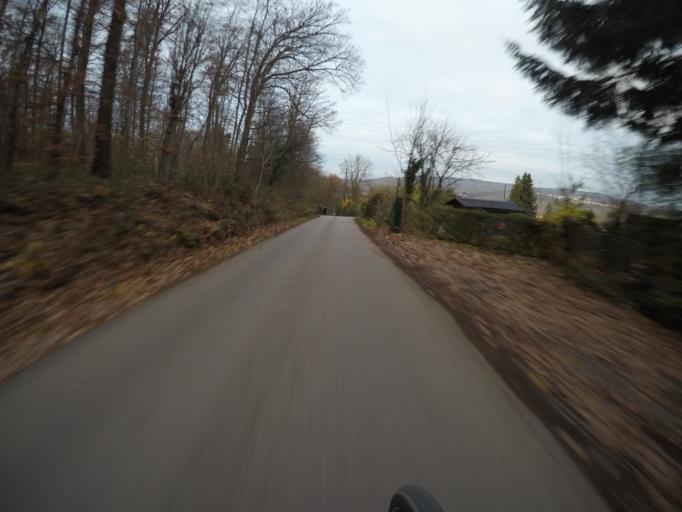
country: DE
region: Baden-Wuerttemberg
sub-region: Regierungsbezirk Stuttgart
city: Ostfildern
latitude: 48.7477
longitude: 9.2560
